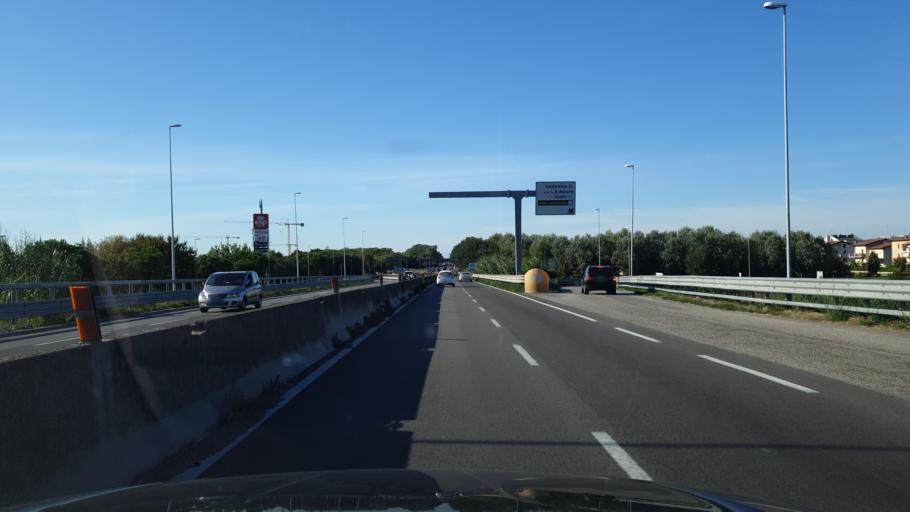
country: IT
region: Emilia-Romagna
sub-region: Provincia di Ravenna
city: Madonna Dell'Albero
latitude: 44.3944
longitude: 12.1842
